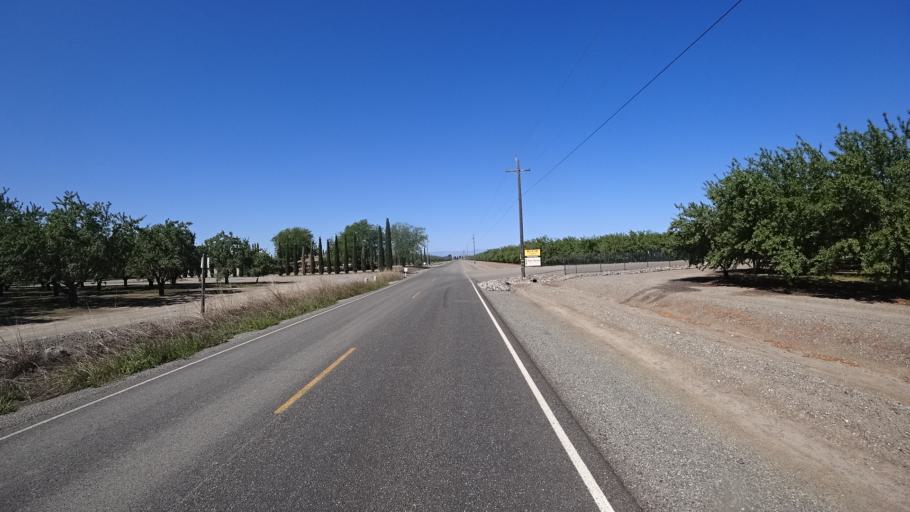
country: US
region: California
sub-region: Glenn County
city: Hamilton City
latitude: 39.7106
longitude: -122.0942
